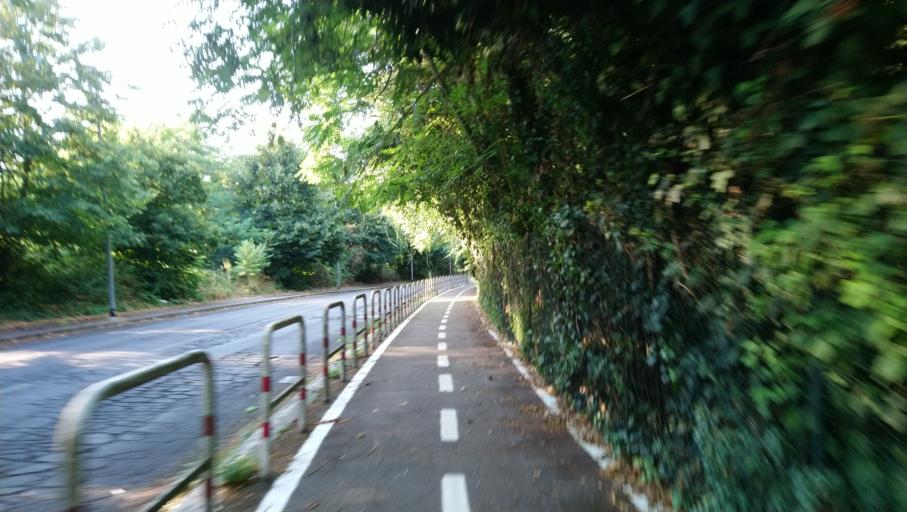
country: IT
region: Latium
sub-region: Citta metropolitana di Roma Capitale
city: Rome
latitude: 41.9376
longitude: 12.4965
